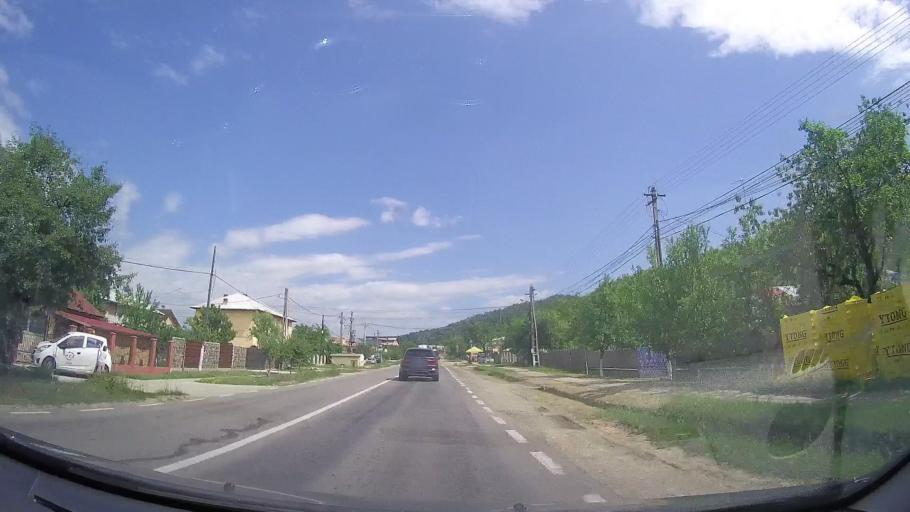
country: RO
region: Prahova
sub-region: Comuna Gura Vitioarei
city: Fagetu
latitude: 45.1227
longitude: 26.0347
